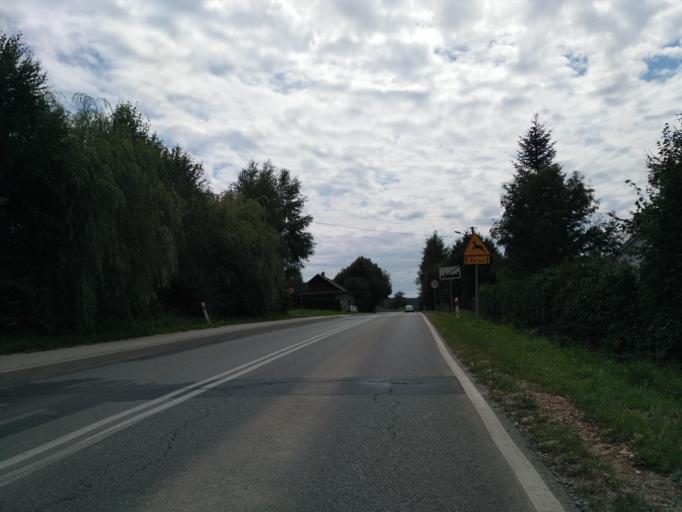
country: PL
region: Subcarpathian Voivodeship
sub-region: Powiat rzeszowski
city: Chmielnik
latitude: 49.9476
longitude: 22.1010
